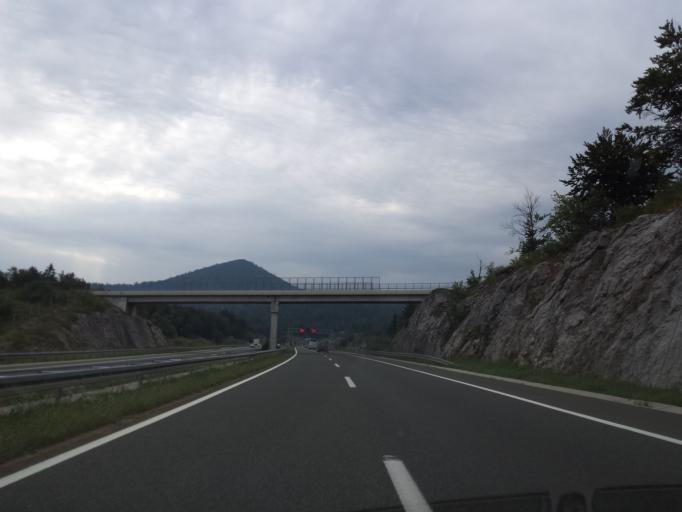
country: HR
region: Karlovacka
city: Ostarije
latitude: 45.1225
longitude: 15.2437
